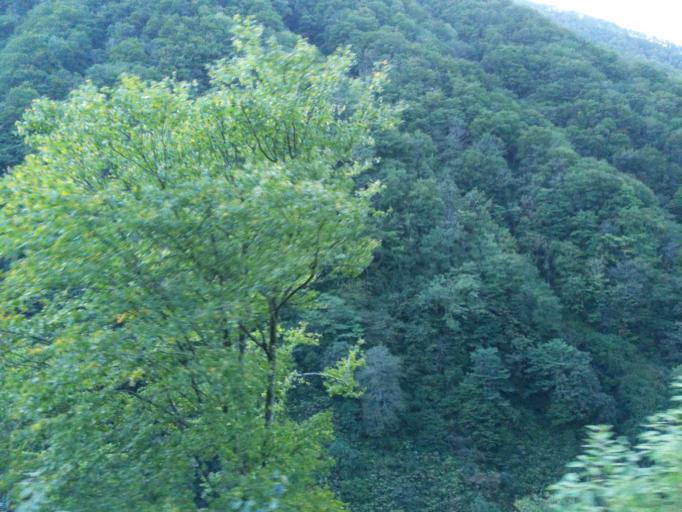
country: JP
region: Toyama
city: Kamiichi
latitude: 36.5207
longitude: 137.4496
